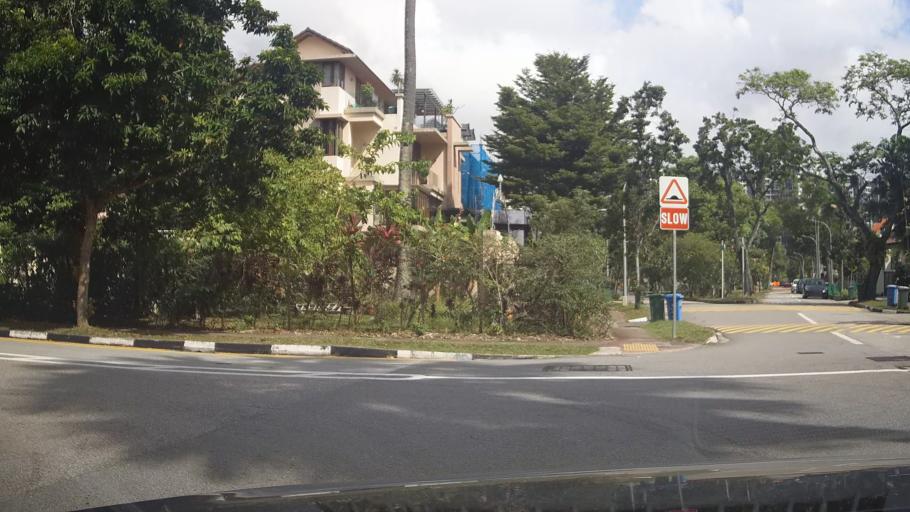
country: SG
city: Singapore
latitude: 1.3022
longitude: 103.8880
